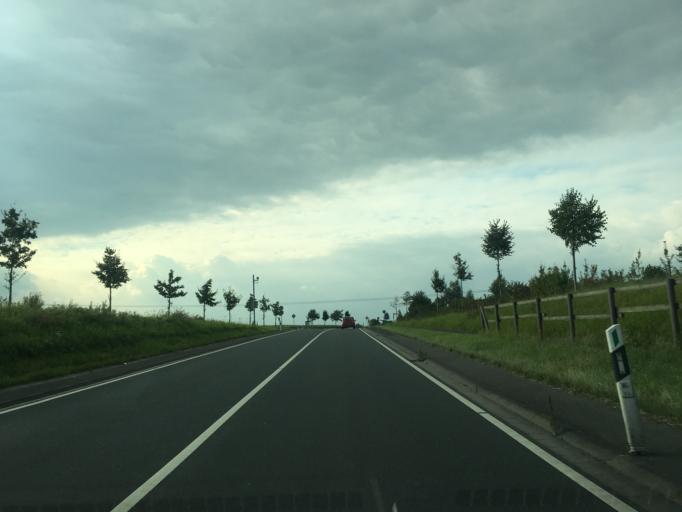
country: DE
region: North Rhine-Westphalia
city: Olfen
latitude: 51.7018
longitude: 7.4085
